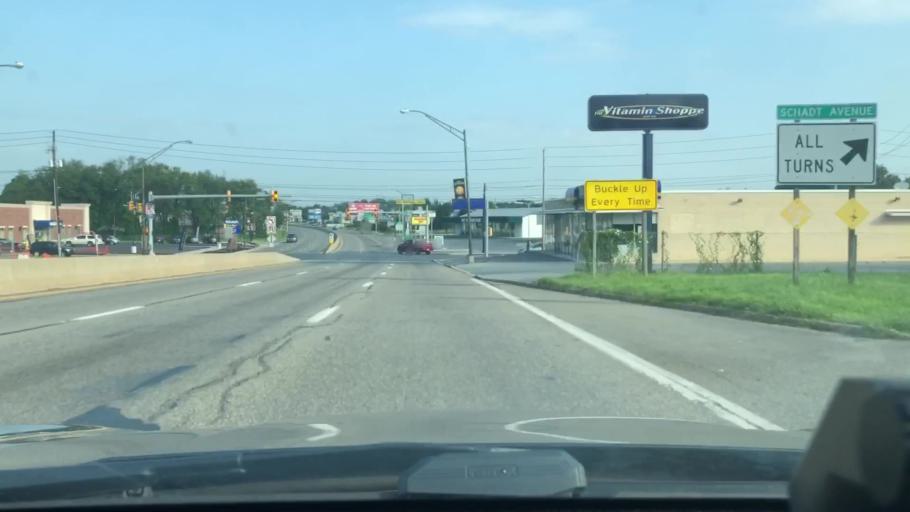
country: US
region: Pennsylvania
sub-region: Lehigh County
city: Fullerton
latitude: 40.6411
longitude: -75.4900
